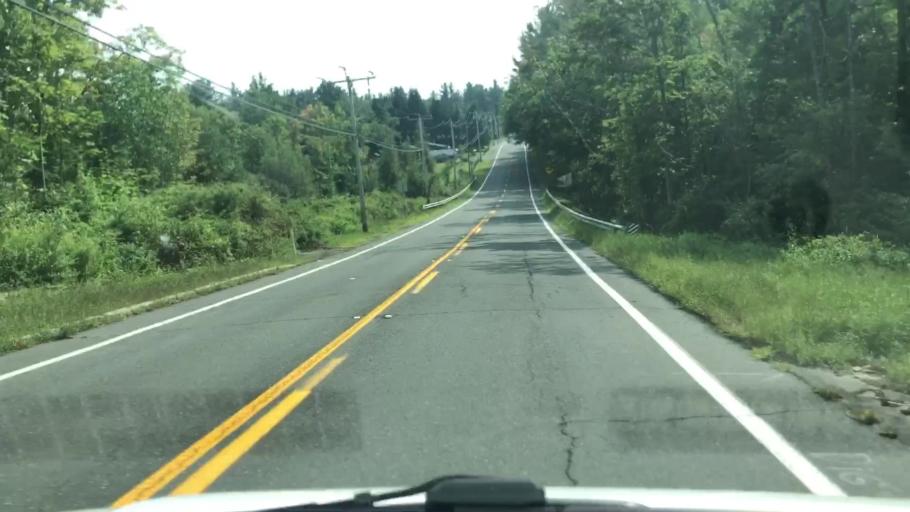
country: US
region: Massachusetts
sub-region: Hampshire County
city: Chesterfield
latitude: 42.4089
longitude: -72.9375
